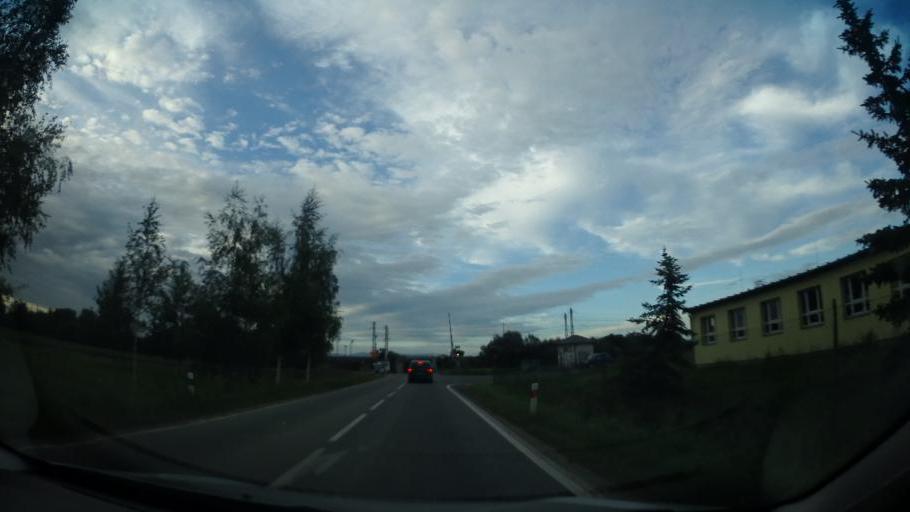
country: CZ
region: Olomoucky
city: Cervenka
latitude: 49.7265
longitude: 17.0812
